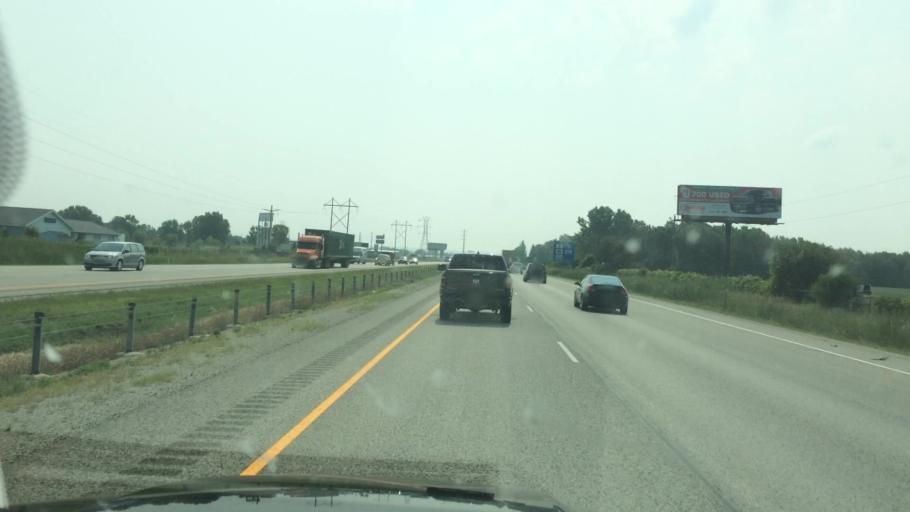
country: US
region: Wisconsin
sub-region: Fond du Lac County
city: North Fond du Lac
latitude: 43.8039
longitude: -88.4957
